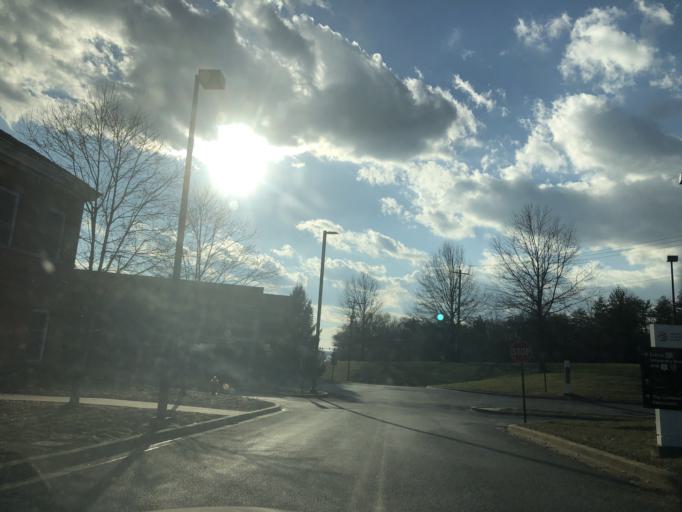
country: US
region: Maryland
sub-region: Prince George's County
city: College Park
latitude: 38.9878
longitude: -76.9540
